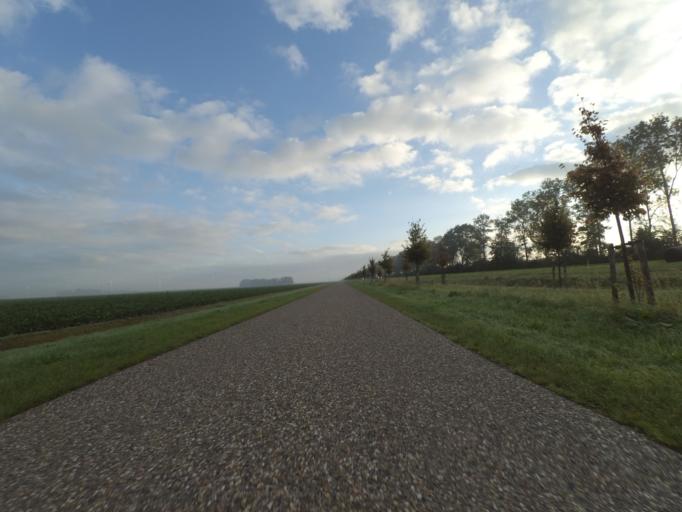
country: NL
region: Flevoland
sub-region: Gemeente Dronten
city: Biddinghuizen
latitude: 52.4386
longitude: 5.6501
